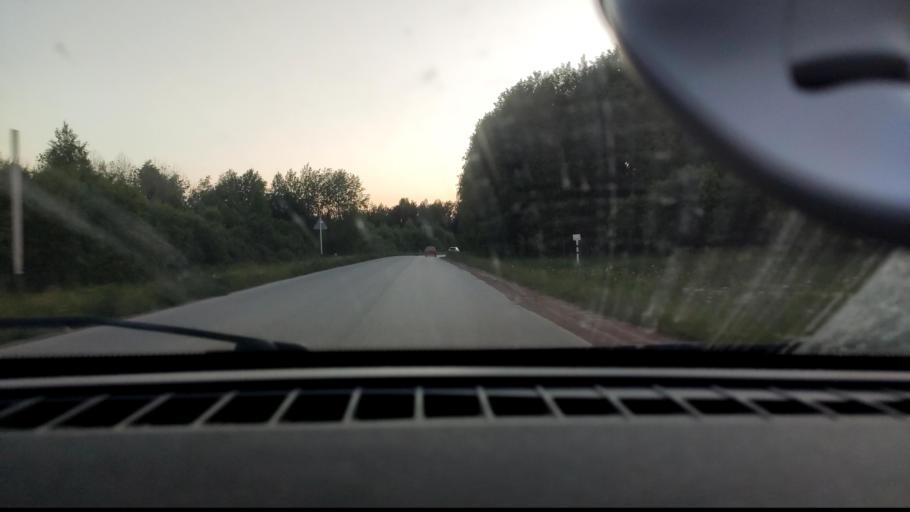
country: RU
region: Perm
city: Polazna
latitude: 58.2020
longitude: 56.4758
